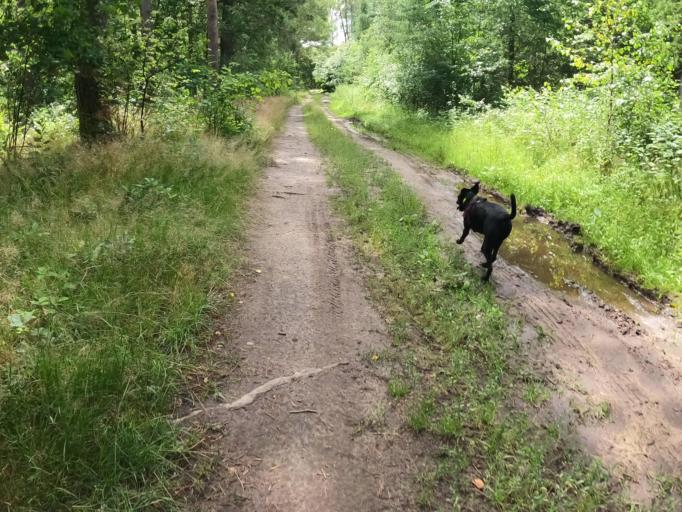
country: PL
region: West Pomeranian Voivodeship
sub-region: Powiat bialogardzki
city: Karlino
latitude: 53.9960
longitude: 15.9198
